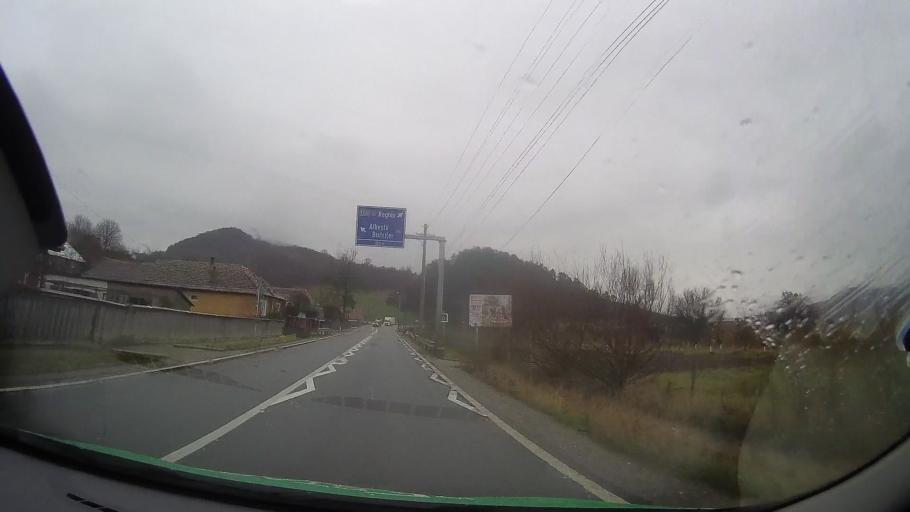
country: RO
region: Bistrita-Nasaud
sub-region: Comuna Galatii Bistritei
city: Galatii Bistritei
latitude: 46.9801
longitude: 24.4354
